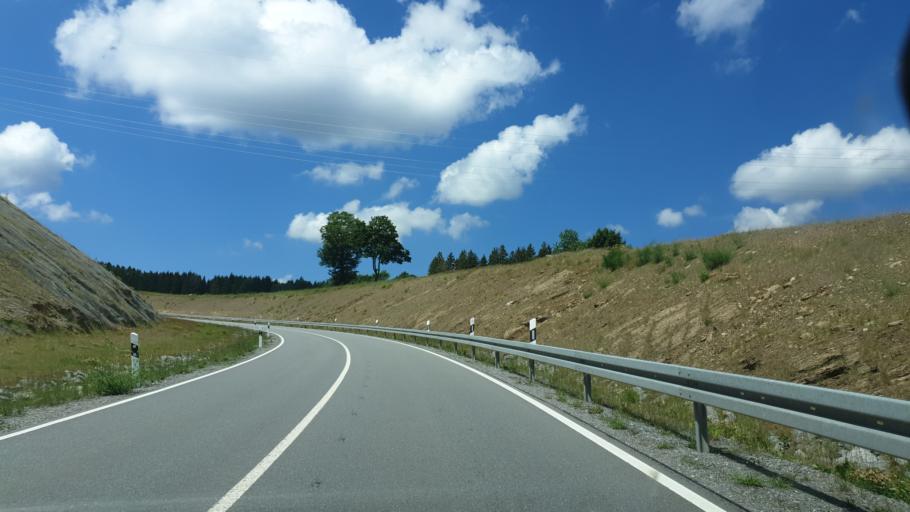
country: DE
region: Saxony
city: Schwarzenberg
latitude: 50.5238
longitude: 12.7637
